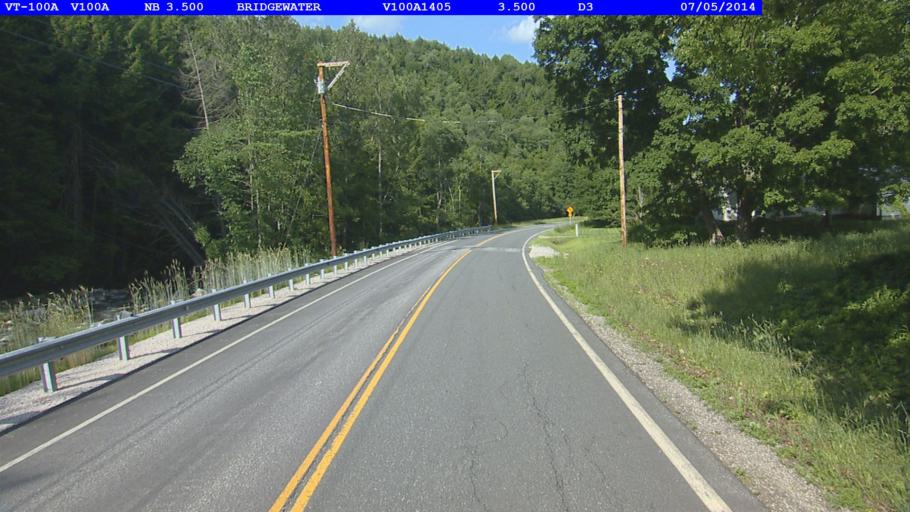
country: US
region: Vermont
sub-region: Windsor County
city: Woodstock
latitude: 43.5621
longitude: -72.6987
